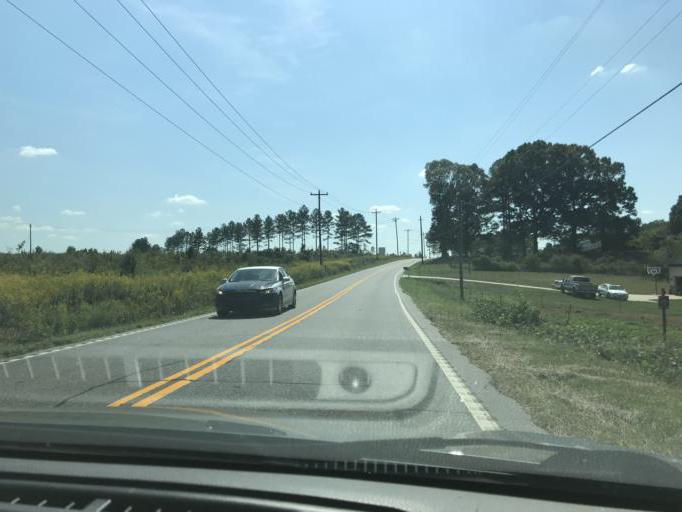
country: US
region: South Carolina
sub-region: Cherokee County
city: Gaffney
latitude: 35.1068
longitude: -81.7031
